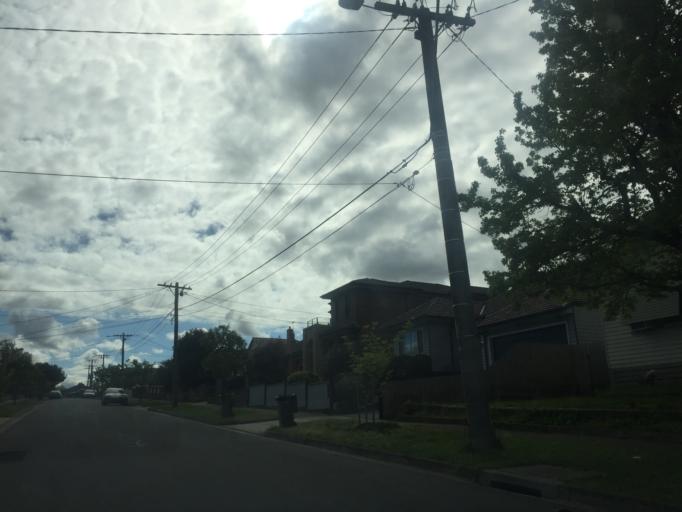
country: AU
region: Victoria
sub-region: Darebin
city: Reservoir
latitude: -37.7267
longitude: 145.0169
